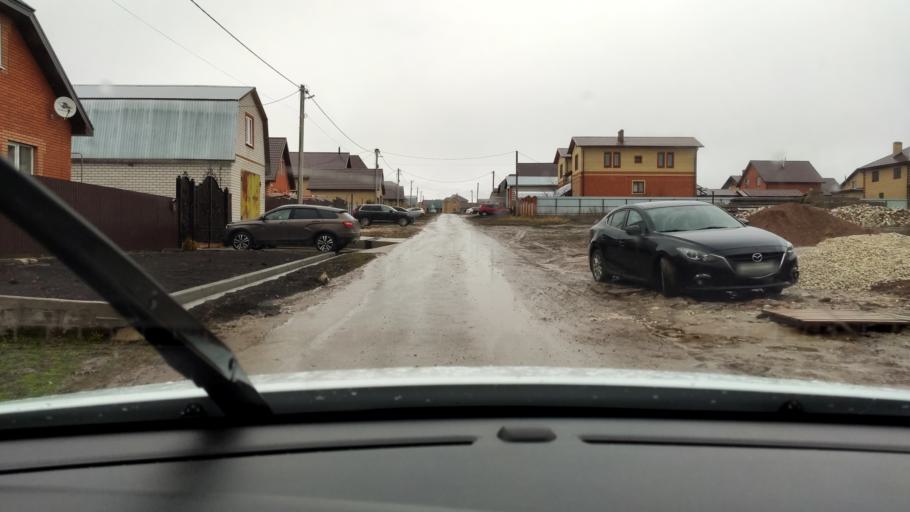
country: RU
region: Tatarstan
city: Vysokaya Gora
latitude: 55.9014
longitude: 49.3160
